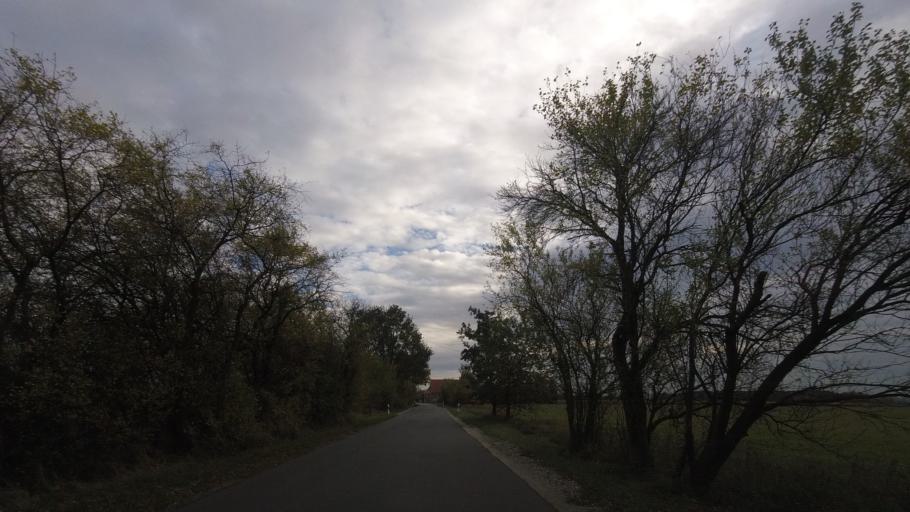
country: DE
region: Brandenburg
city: Borkheide
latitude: 52.1941
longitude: 12.9137
